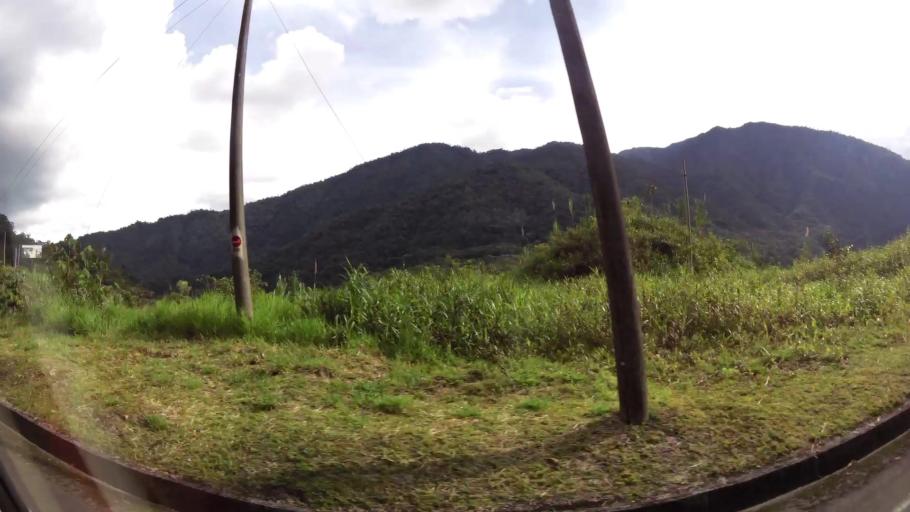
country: EC
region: Pastaza
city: Puyo
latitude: -1.4457
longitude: -78.1628
